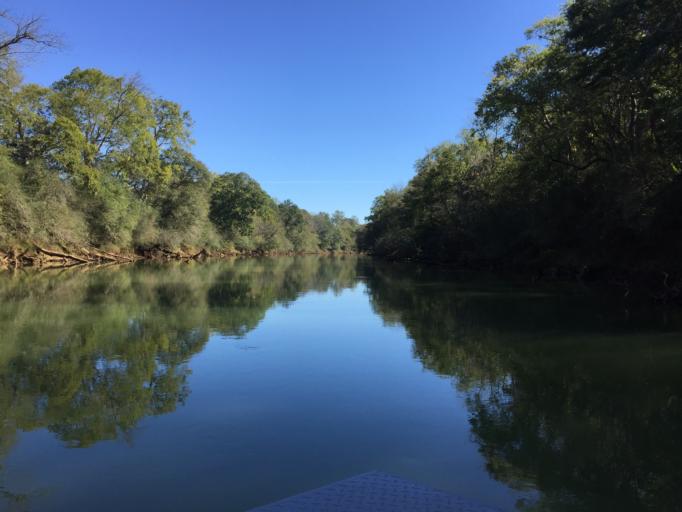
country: US
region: Georgia
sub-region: Gwinnett County
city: Duluth
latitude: 34.0317
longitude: -84.1330
